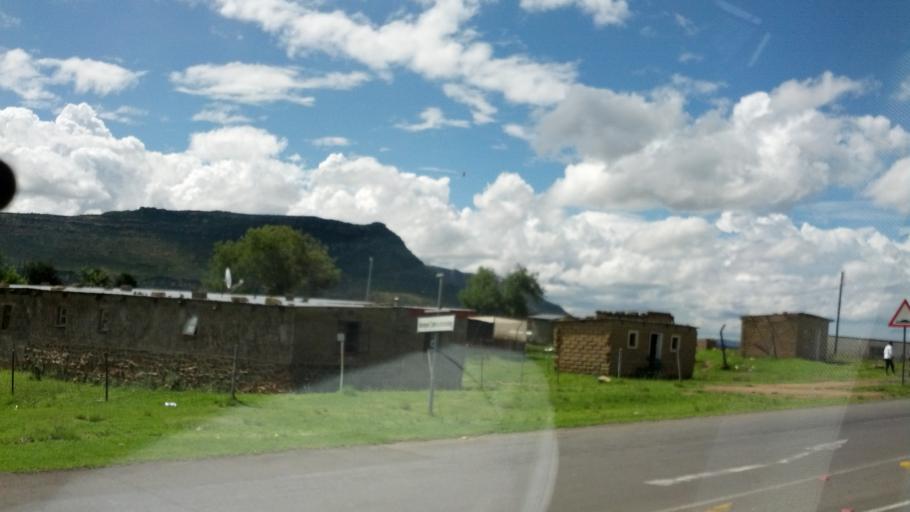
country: LS
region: Maseru
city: Maseru
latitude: -29.5425
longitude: 27.5082
